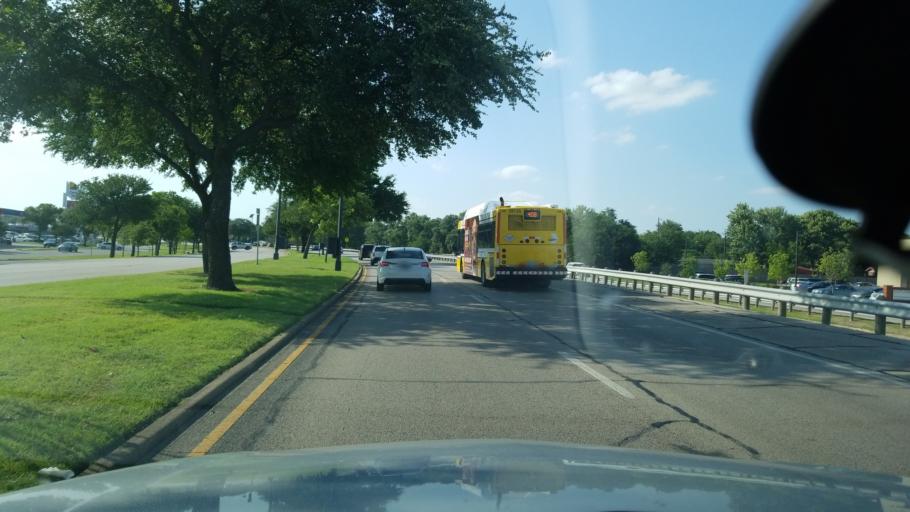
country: US
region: Texas
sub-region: Dallas County
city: Irving
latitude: 32.8231
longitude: -96.9668
